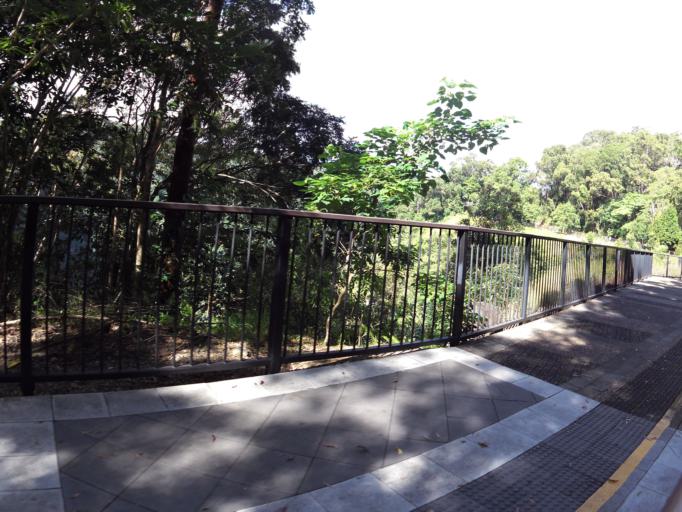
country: AU
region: Queensland
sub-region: Tablelands
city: Kuranda
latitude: -16.8357
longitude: 145.6426
